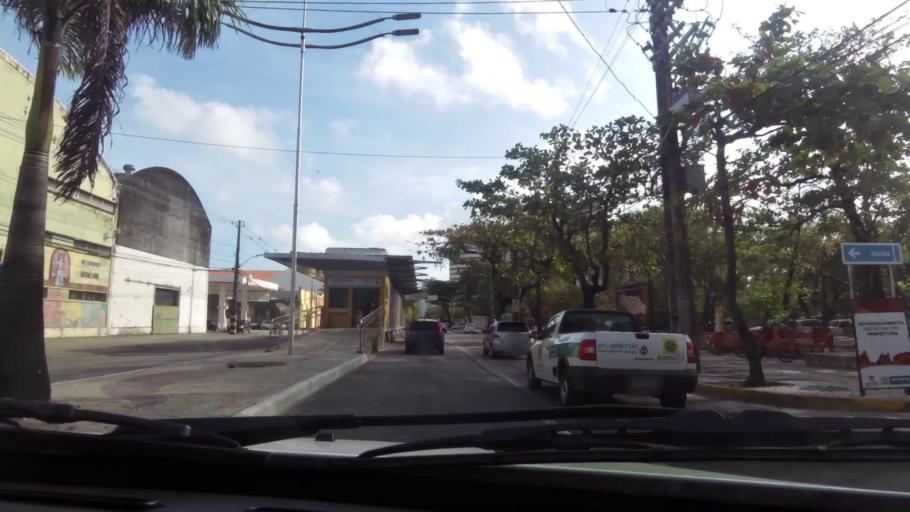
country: BR
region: Pernambuco
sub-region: Recife
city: Recife
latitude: -8.0570
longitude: -34.8723
